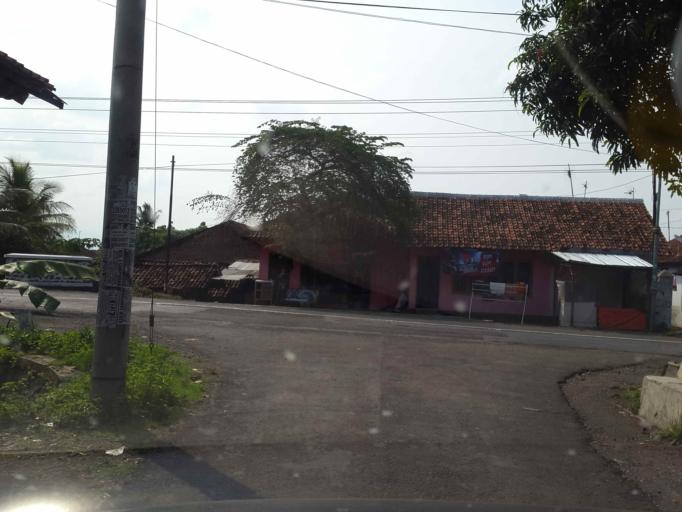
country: ID
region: Central Java
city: Balapulang
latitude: -7.0754
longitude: 109.0876
